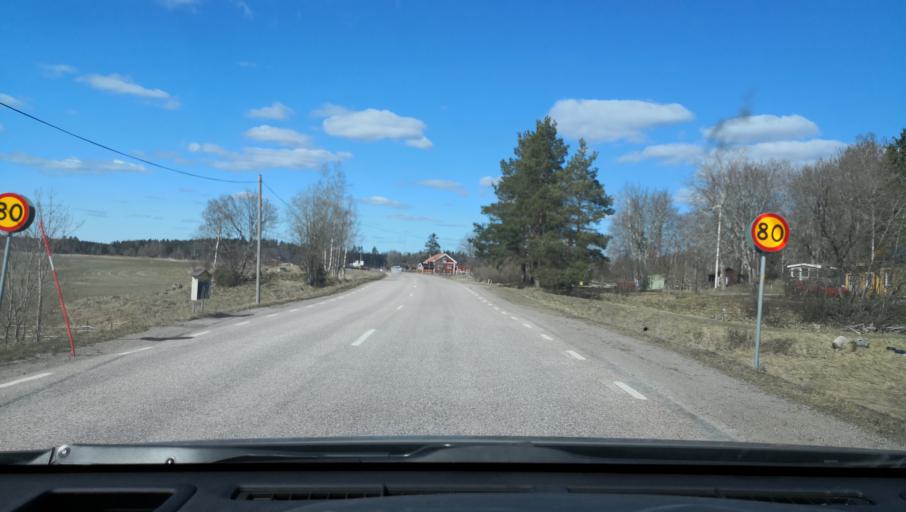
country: SE
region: Vaestmanland
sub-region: Sala Kommun
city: Sala
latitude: 59.9876
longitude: 16.6444
